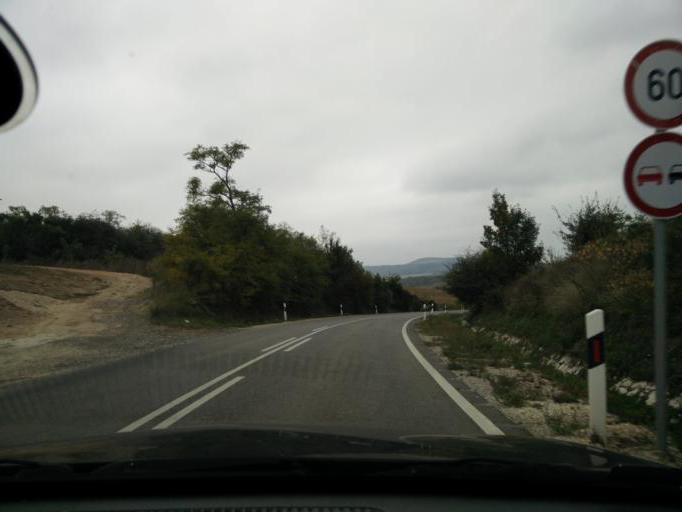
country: HU
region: Komarom-Esztergom
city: Bajna
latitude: 47.6864
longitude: 18.6086
